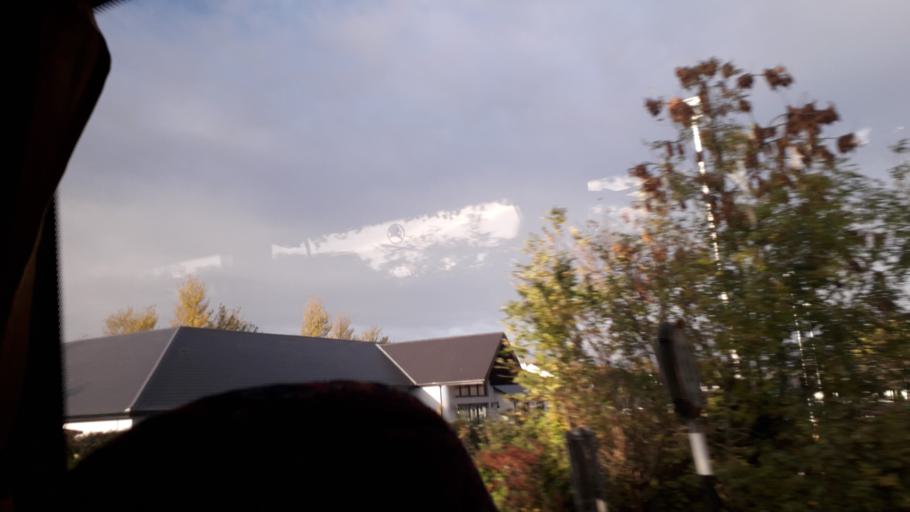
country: IE
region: Leinster
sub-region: Kildare
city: Maynooth
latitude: 53.3593
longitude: -6.5932
